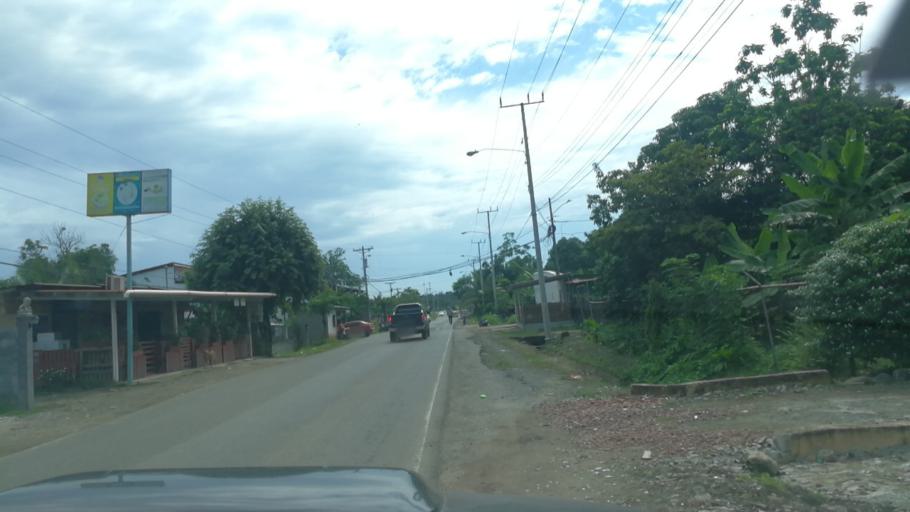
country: PA
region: Panama
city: Paso Blanco
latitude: 9.1191
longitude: -79.2572
